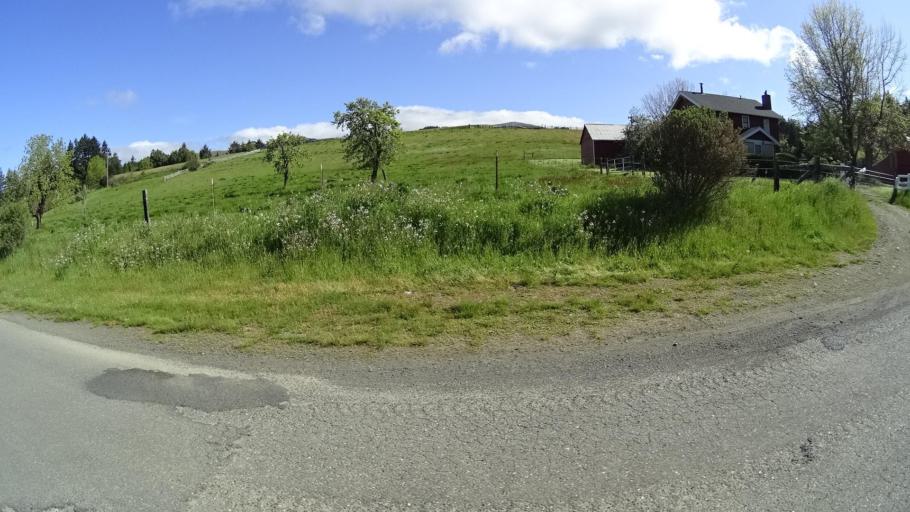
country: US
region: California
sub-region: Humboldt County
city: Ferndale
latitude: 40.3425
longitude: -124.3205
